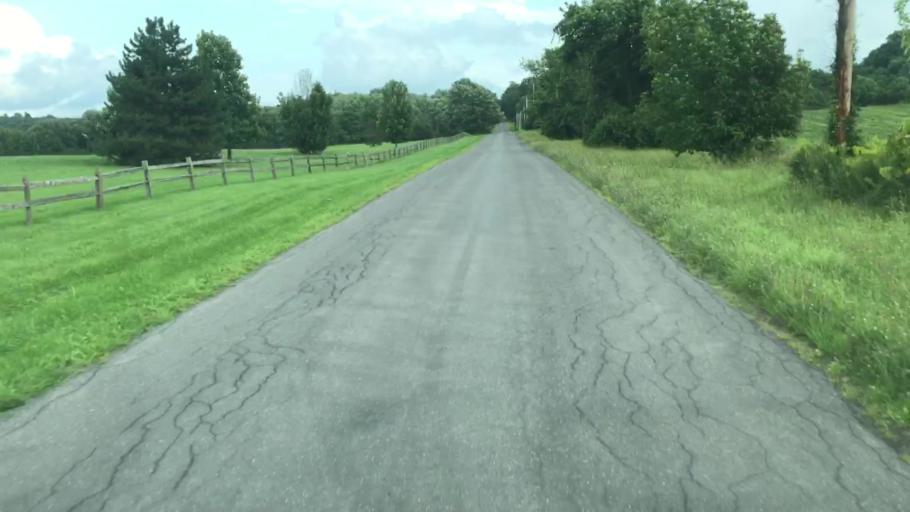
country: US
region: New York
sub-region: Onondaga County
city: Elbridge
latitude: 42.9861
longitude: -76.4609
